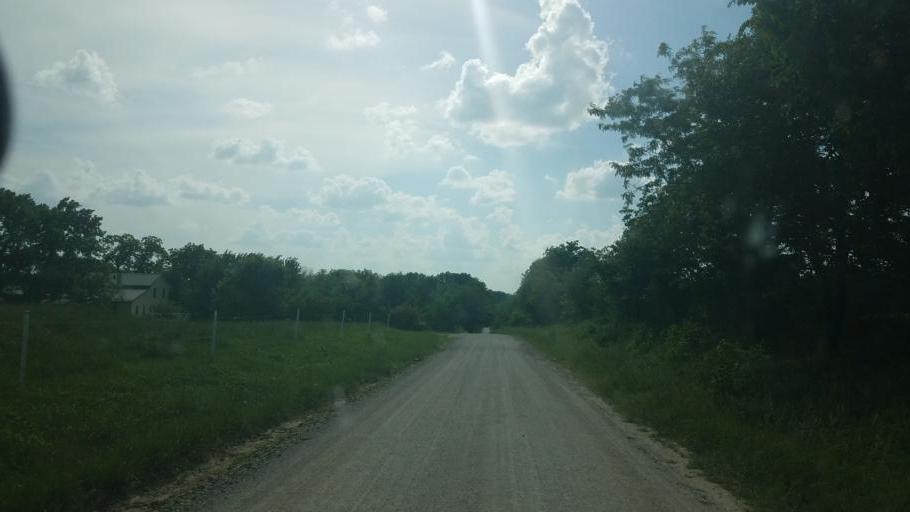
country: US
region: Missouri
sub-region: Cooper County
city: Boonville
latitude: 38.8503
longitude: -92.6376
